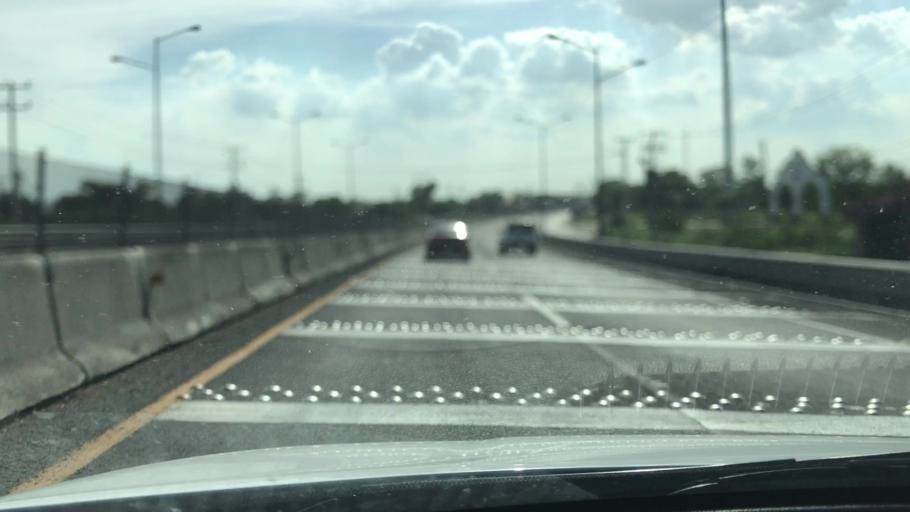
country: MX
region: Guanajuato
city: Villagran
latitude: 20.5082
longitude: -100.9942
